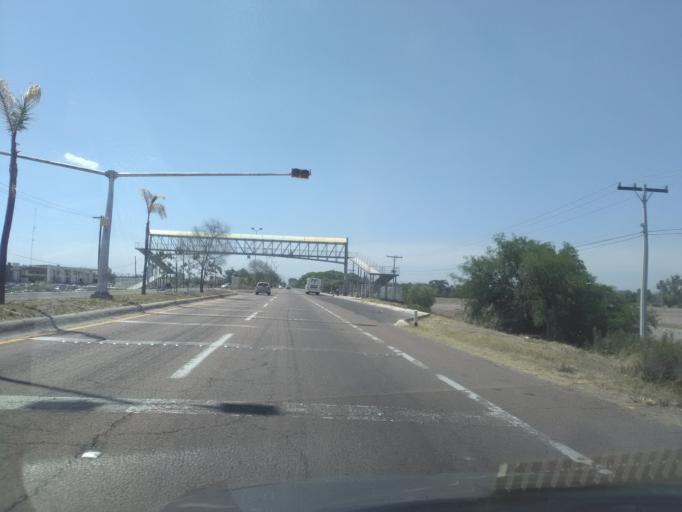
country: MX
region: Durango
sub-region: Durango
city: Jose Refugio Salcido
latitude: 24.0240
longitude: -104.5519
